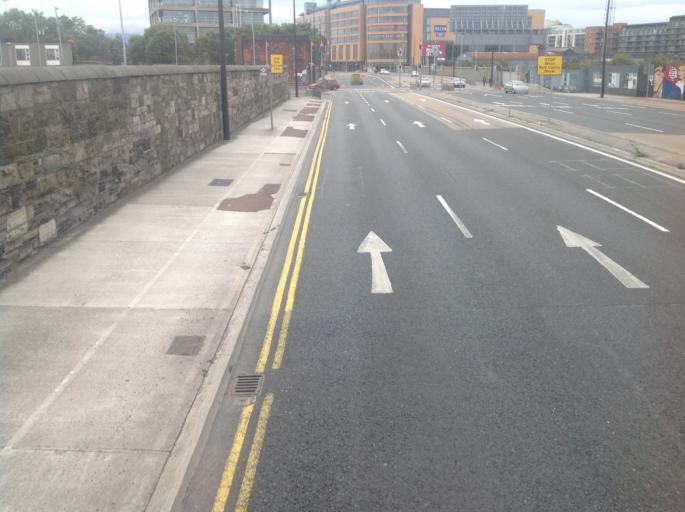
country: IE
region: Leinster
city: Ringsend
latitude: 53.3521
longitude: -6.2251
